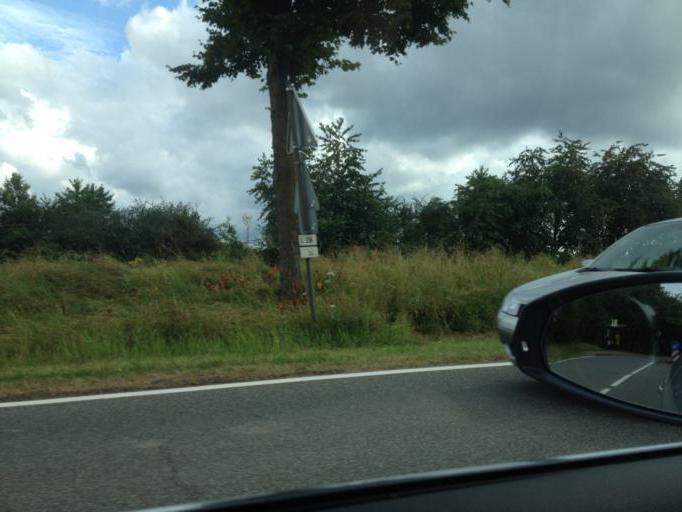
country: DE
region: Saarland
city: Schiffweiler
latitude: 49.3635
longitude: 7.1193
